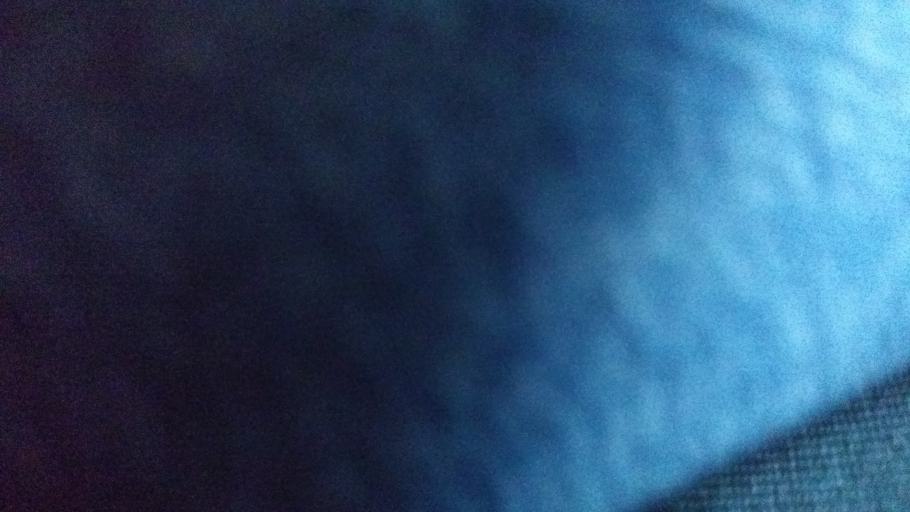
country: MX
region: Yucatan
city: Itzincab Palomeque
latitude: 20.9293
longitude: -89.6676
